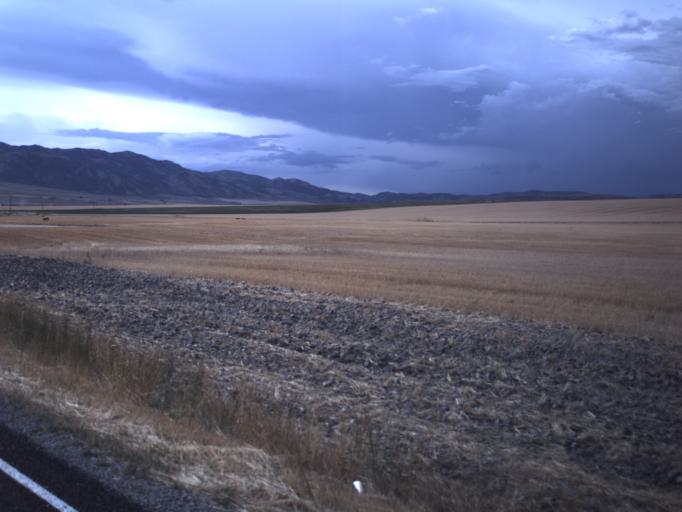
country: US
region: Utah
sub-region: Cache County
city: Benson
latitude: 41.9174
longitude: -111.9991
